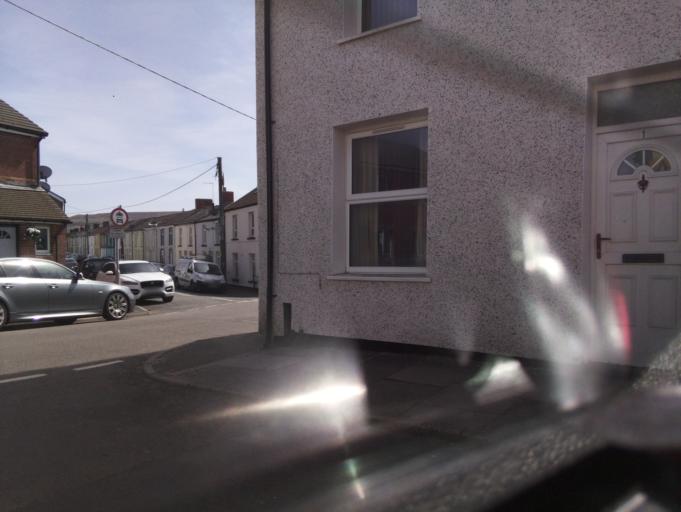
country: GB
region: Wales
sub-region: Merthyr Tydfil County Borough
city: Merthyr Tydfil
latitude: 51.7668
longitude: -3.3527
